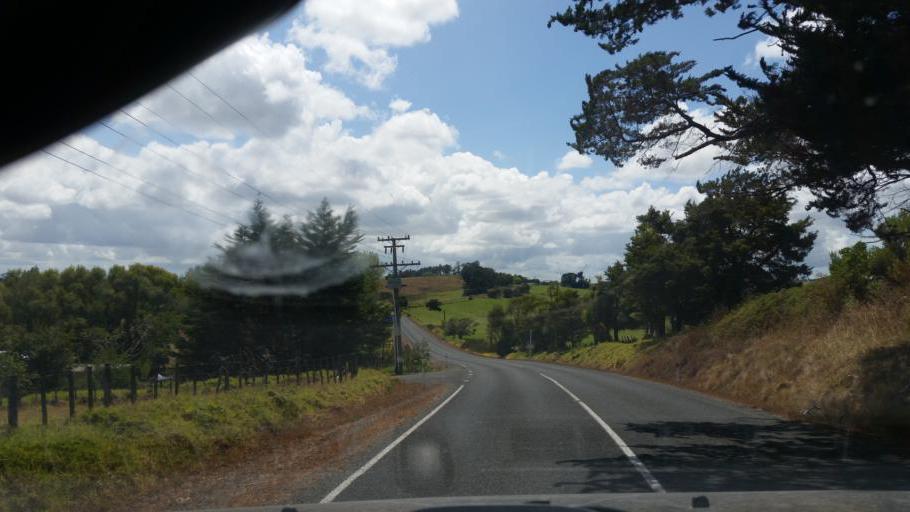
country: NZ
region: Northland
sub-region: Whangarei
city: Ruakaka
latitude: -36.1378
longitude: 174.2260
